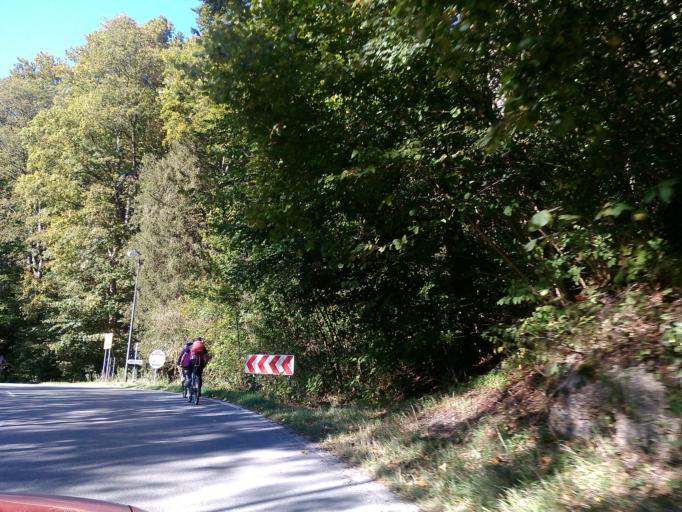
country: DE
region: Bavaria
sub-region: Upper Bavaria
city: Starnberg
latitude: 48.0329
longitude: 11.3605
